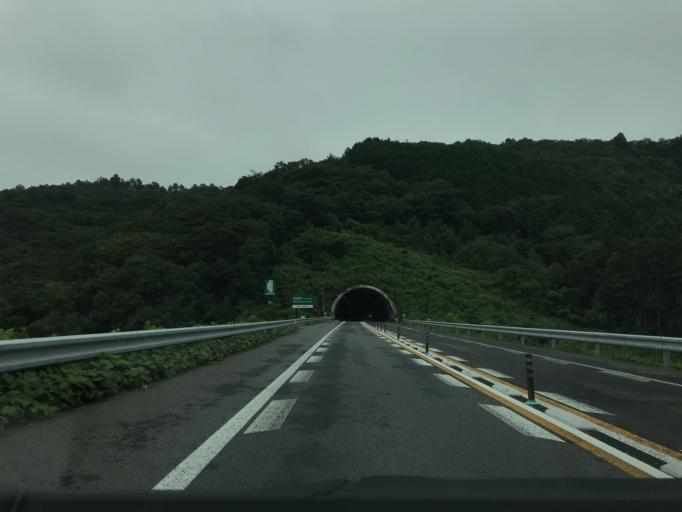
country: JP
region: Fukuoka
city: Nakatsu
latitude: 33.5175
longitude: 131.2695
